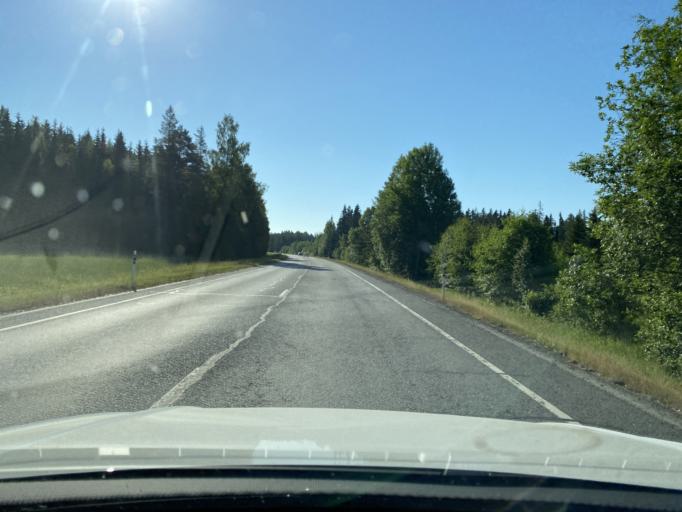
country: FI
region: Haeme
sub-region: Forssa
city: Tammela
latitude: 60.8272
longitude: 23.7393
